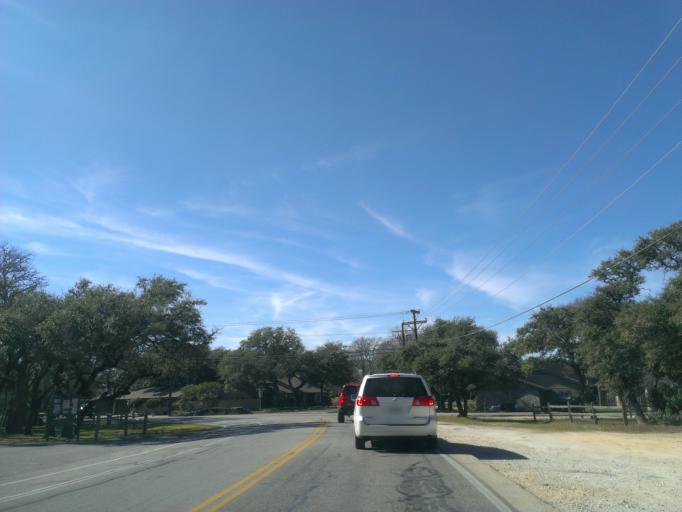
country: US
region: Texas
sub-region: Travis County
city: Lakeway
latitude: 30.3678
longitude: -97.9810
